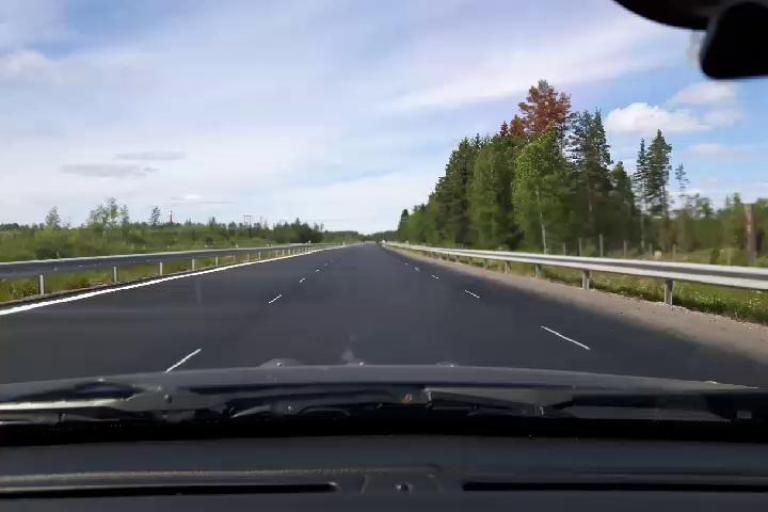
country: SE
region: Gaevleborg
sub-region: Gavle Kommun
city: Gavle
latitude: 60.6239
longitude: 17.1570
